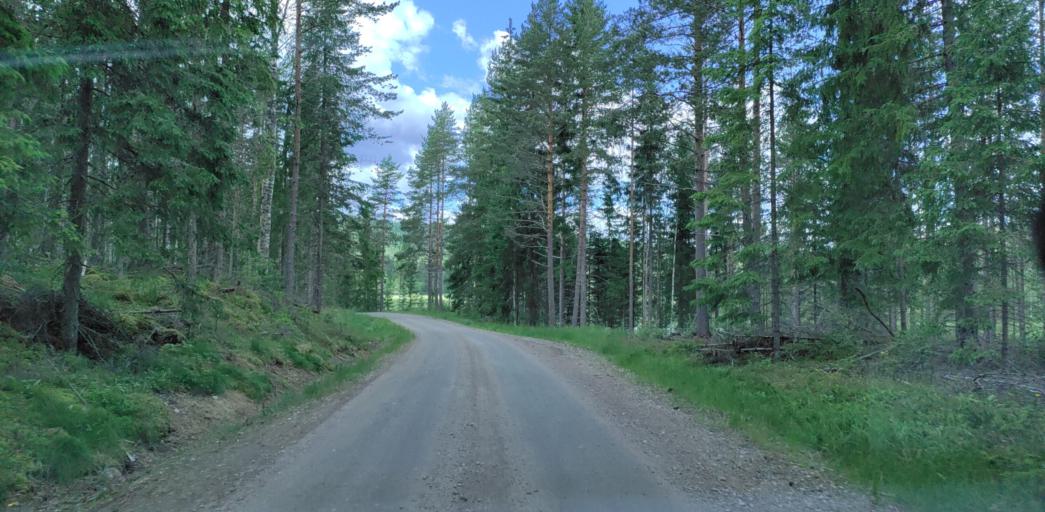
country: SE
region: Vaermland
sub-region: Hagfors Kommun
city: Ekshaerad
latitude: 60.1013
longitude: 13.3673
